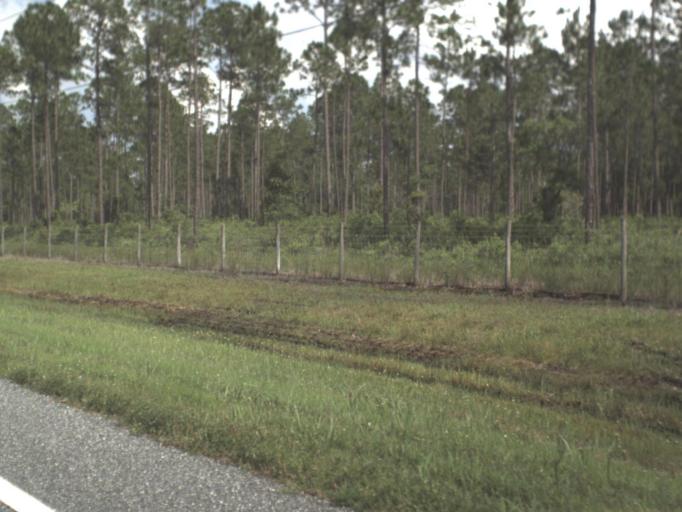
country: US
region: Florida
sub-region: Clay County
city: Middleburg
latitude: 29.9783
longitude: -81.9130
